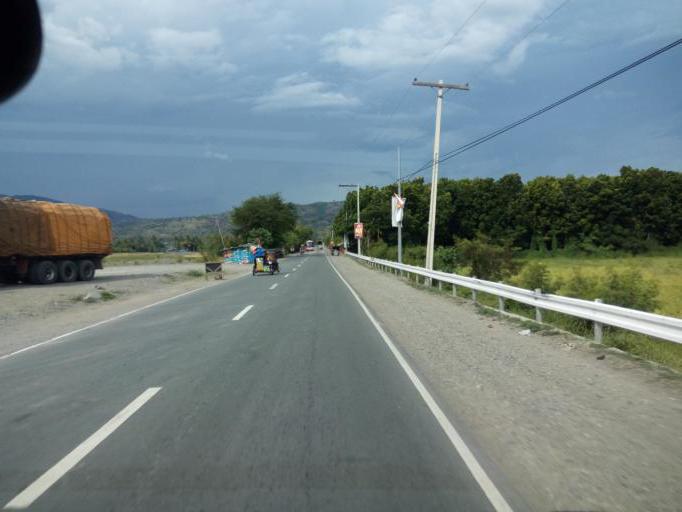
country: PH
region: Central Luzon
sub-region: Province of Nueva Ecija
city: Tayabo
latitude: 15.8252
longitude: 121.0164
